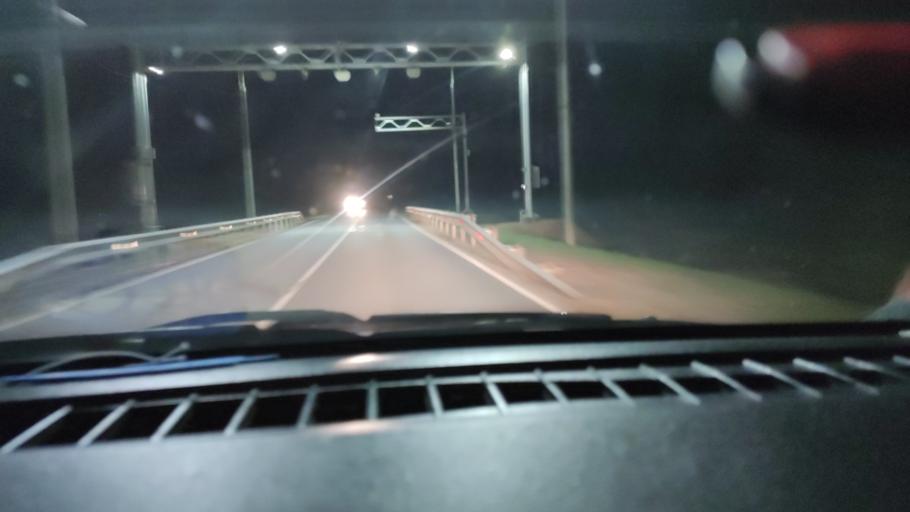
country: RU
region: Saratov
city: Privolzhskiy
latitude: 51.3231
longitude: 46.0279
